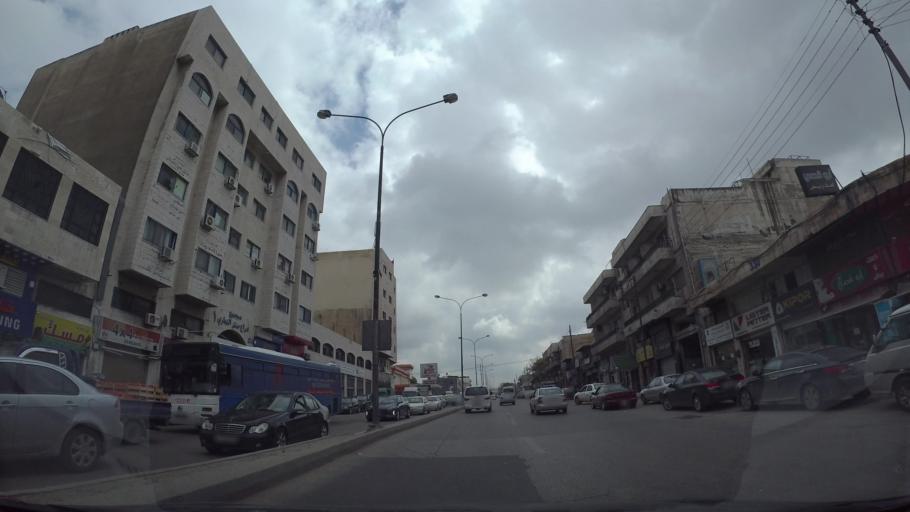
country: JO
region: Amman
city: Al Quwaysimah
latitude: 31.9199
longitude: 35.9383
